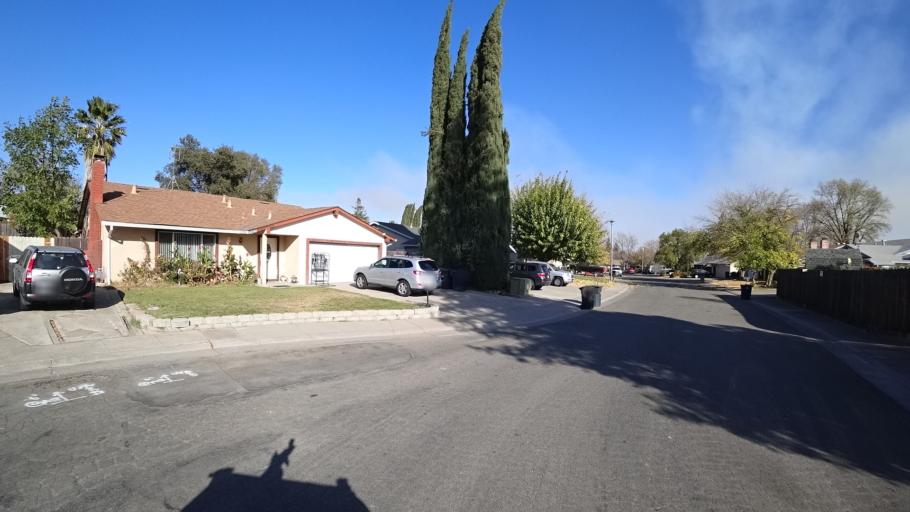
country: US
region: California
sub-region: Sacramento County
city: Antelope
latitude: 38.7003
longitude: -121.3223
